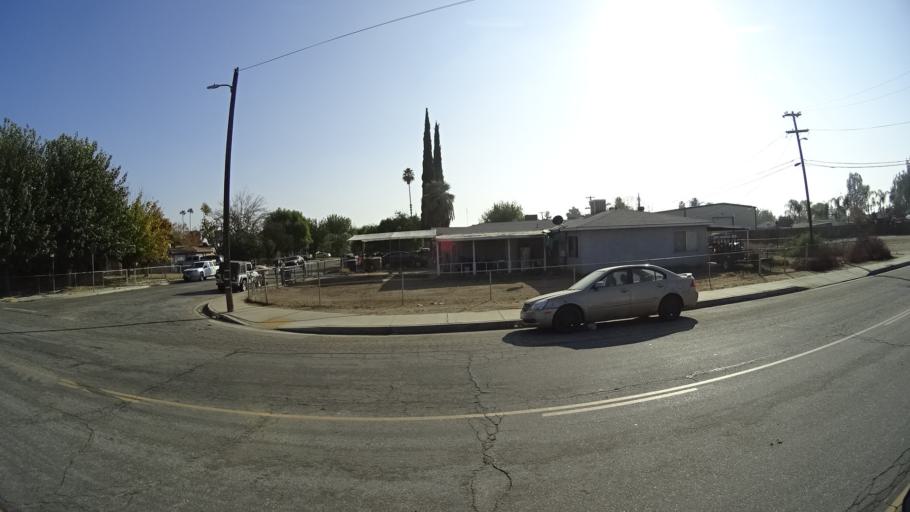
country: US
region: California
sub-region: Kern County
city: Greenfield
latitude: 35.2741
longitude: -119.0090
